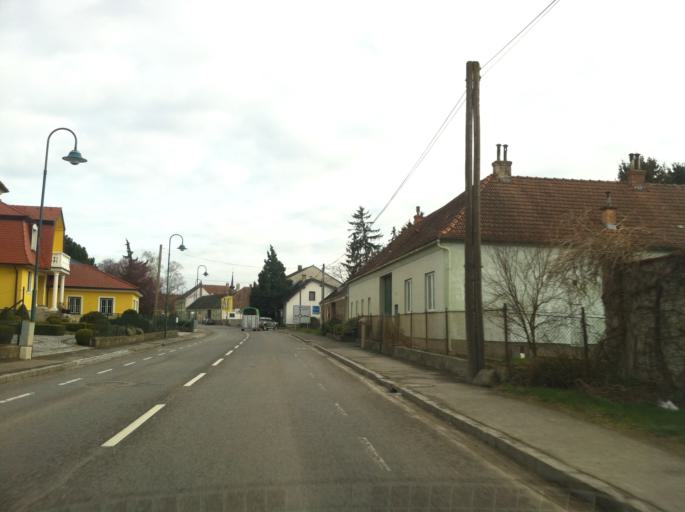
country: AT
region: Lower Austria
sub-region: Politischer Bezirk Tulln
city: Tulln
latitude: 48.3012
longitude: 16.0601
